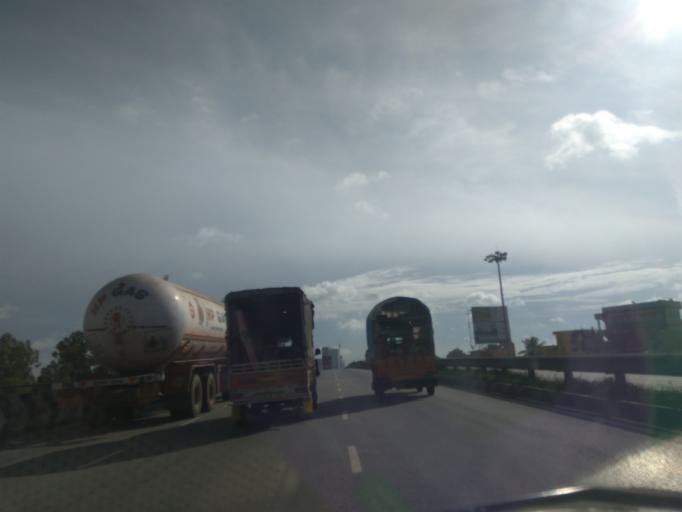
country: IN
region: Karnataka
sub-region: Bangalore Rural
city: Hoskote
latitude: 13.0455
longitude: 77.7495
